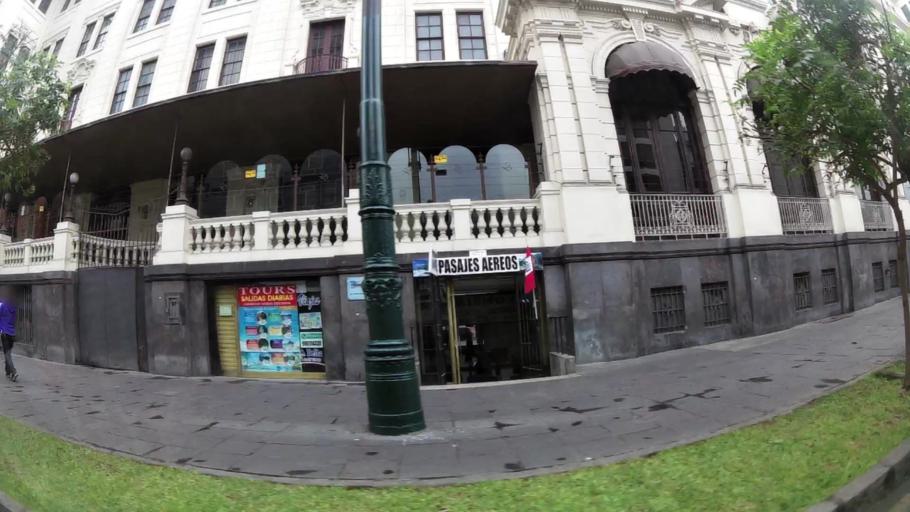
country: PE
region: Lima
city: Lima
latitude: -12.0509
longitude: -77.0358
